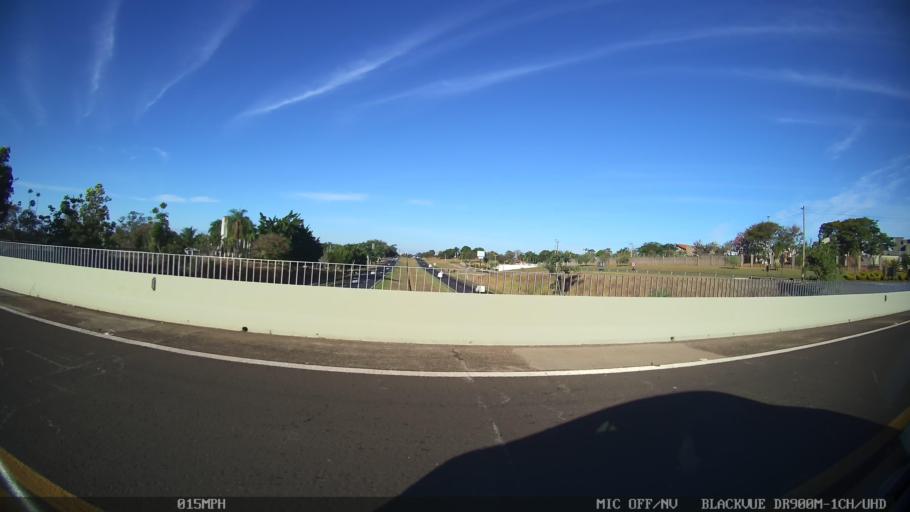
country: BR
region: Sao Paulo
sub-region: Sao Jose Do Rio Preto
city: Sao Jose do Rio Preto
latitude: -20.8162
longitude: -49.4494
